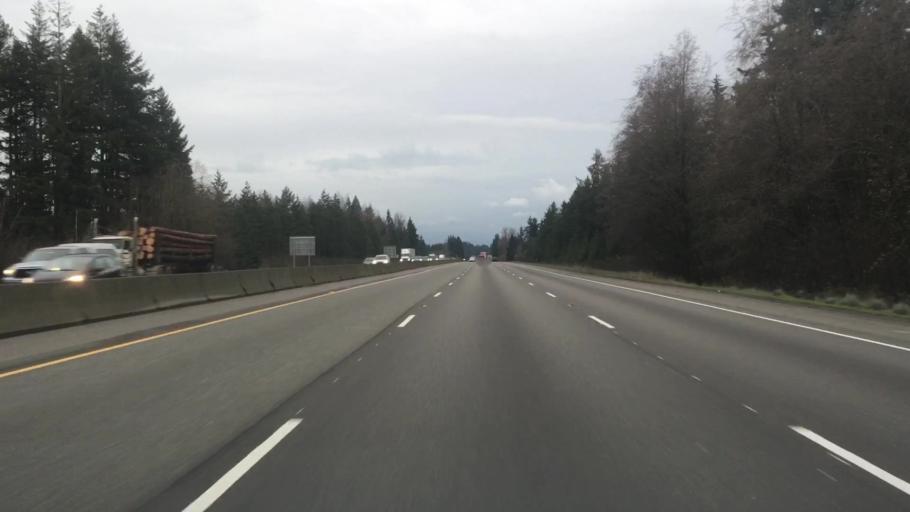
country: US
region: Washington
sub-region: Thurston County
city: Tumwater
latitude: 46.9371
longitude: -122.9422
